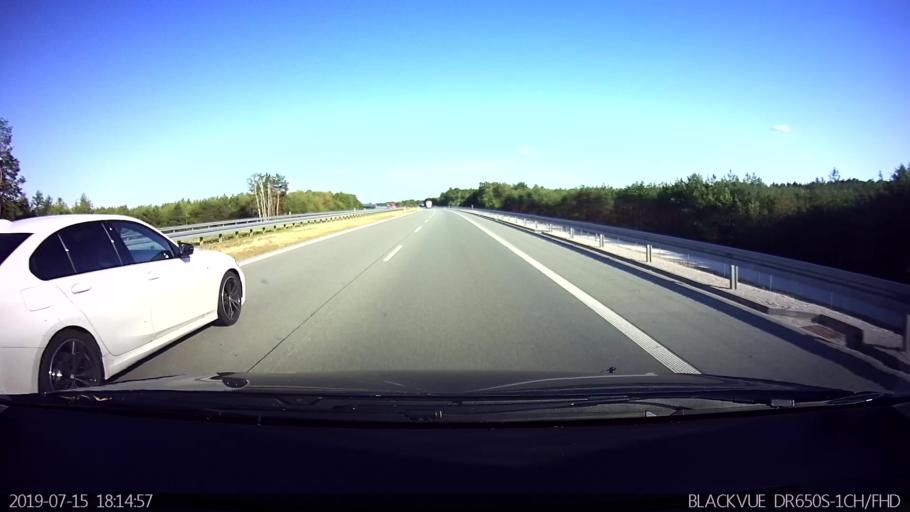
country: PL
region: Lodz Voivodeship
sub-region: Powiat zdunskowolski
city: Zdunska Wola
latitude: 51.5857
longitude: 18.8986
